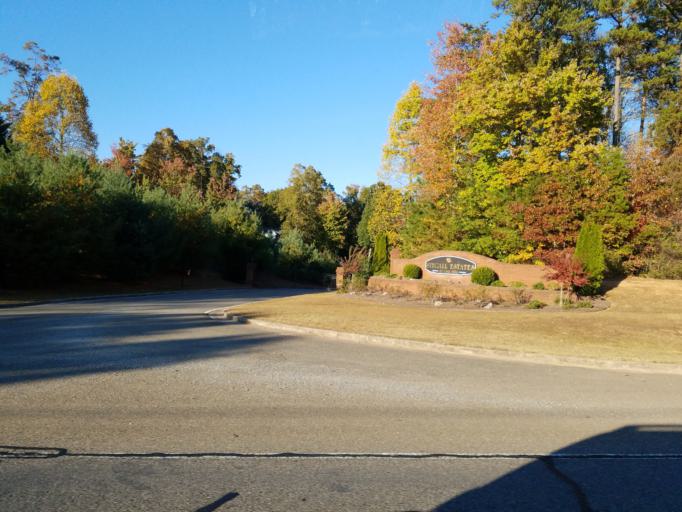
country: US
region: Georgia
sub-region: Gilmer County
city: Ellijay
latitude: 34.6510
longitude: -84.4319
